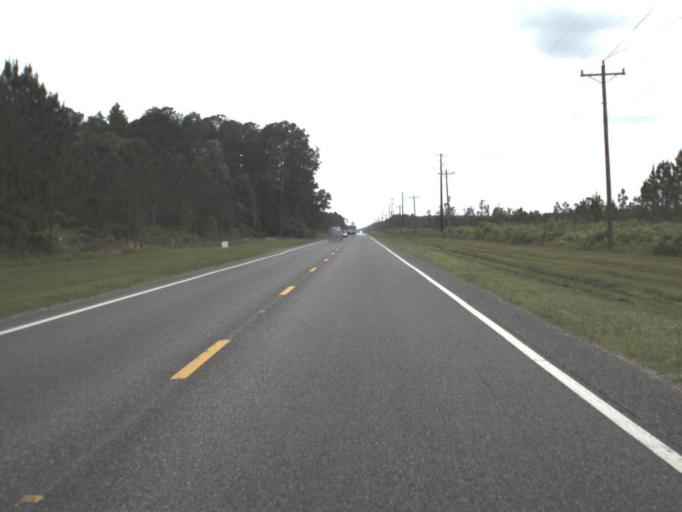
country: US
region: Florida
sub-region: Clay County
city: Middleburg
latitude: 29.9995
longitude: -81.8977
